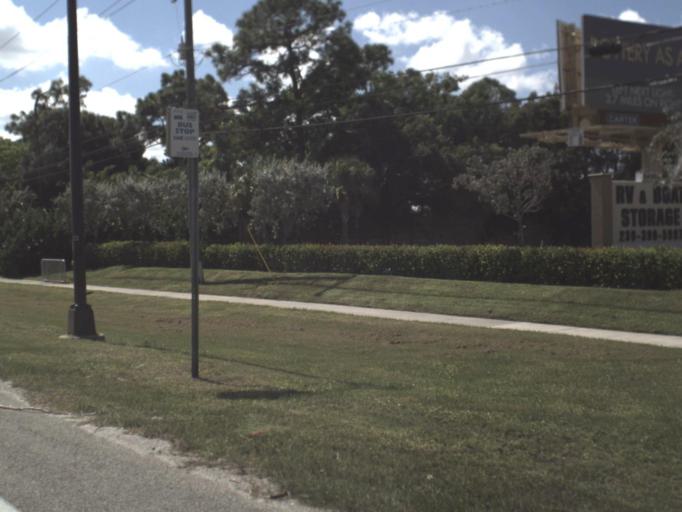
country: US
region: Florida
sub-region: Lee County
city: Estero
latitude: 26.3863
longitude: -81.8090
